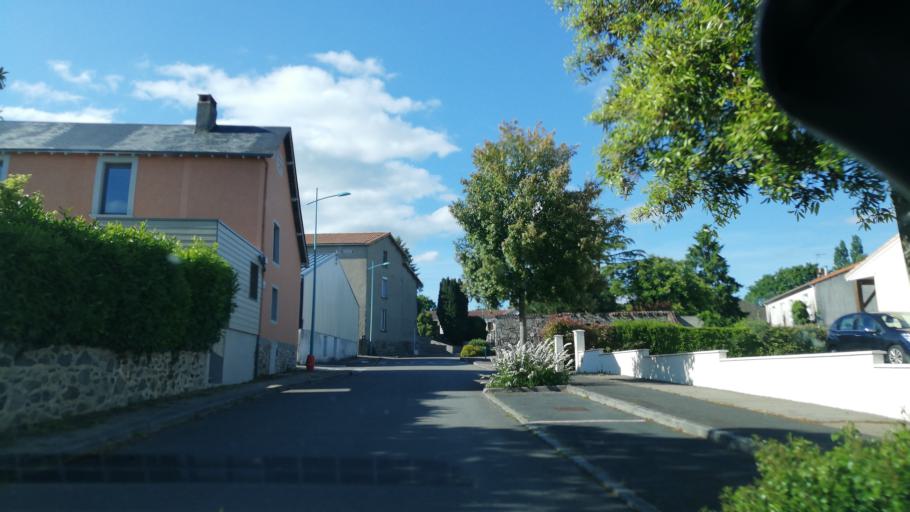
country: FR
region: Poitou-Charentes
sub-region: Departement des Deux-Sevres
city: Moncoutant
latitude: 46.7171
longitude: -0.5876
